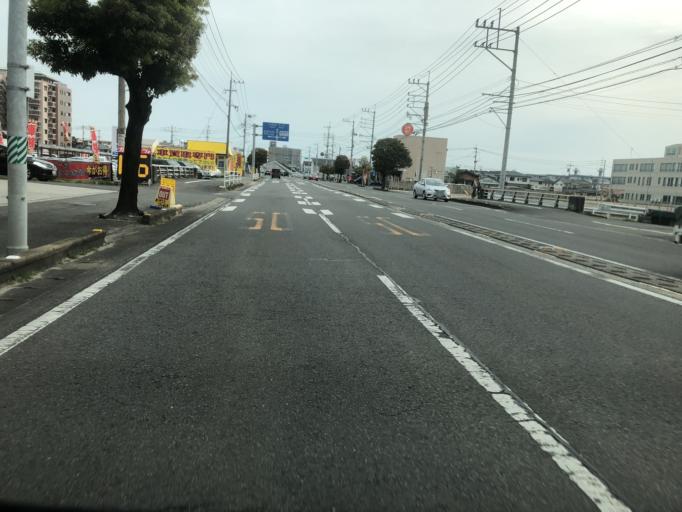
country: JP
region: Saga Prefecture
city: Saga-shi
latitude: 33.2633
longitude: 130.2724
